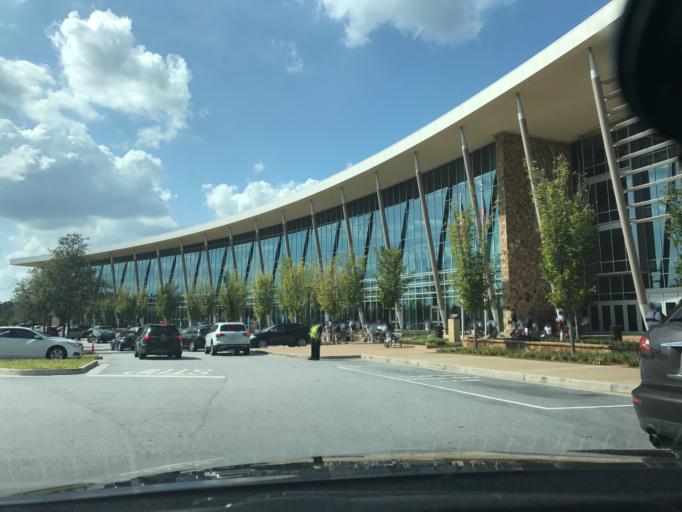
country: US
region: Georgia
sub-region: DeKalb County
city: Decatur
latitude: 33.7458
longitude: -84.3106
